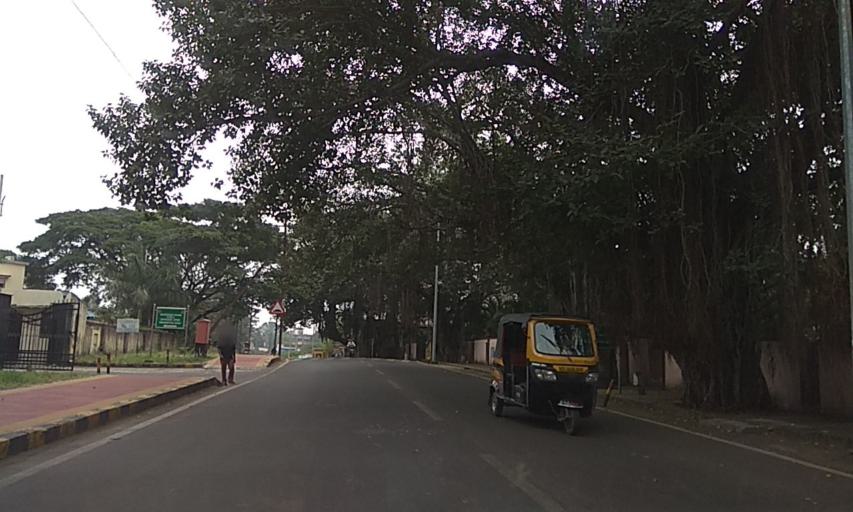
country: IN
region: Maharashtra
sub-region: Pune Division
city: Khadki
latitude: 18.5538
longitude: 73.8529
